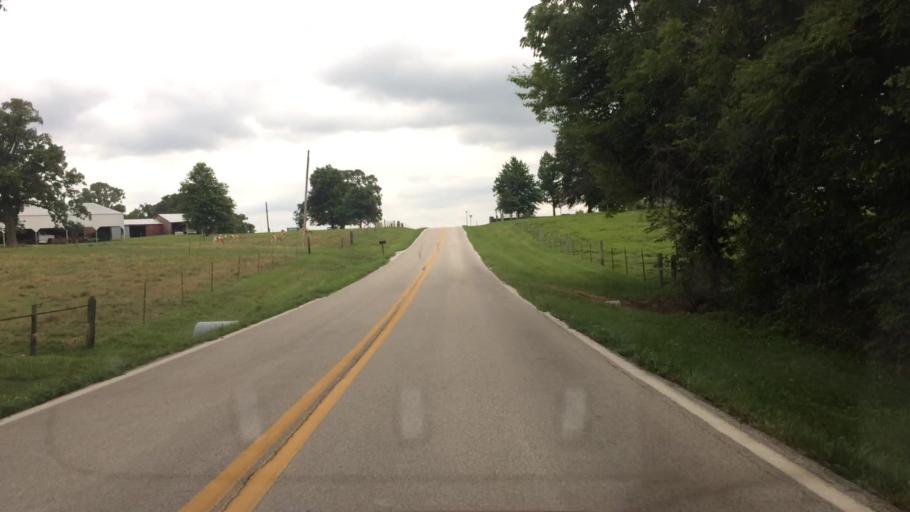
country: US
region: Missouri
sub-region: Greene County
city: Strafford
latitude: 37.3025
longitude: -93.0772
